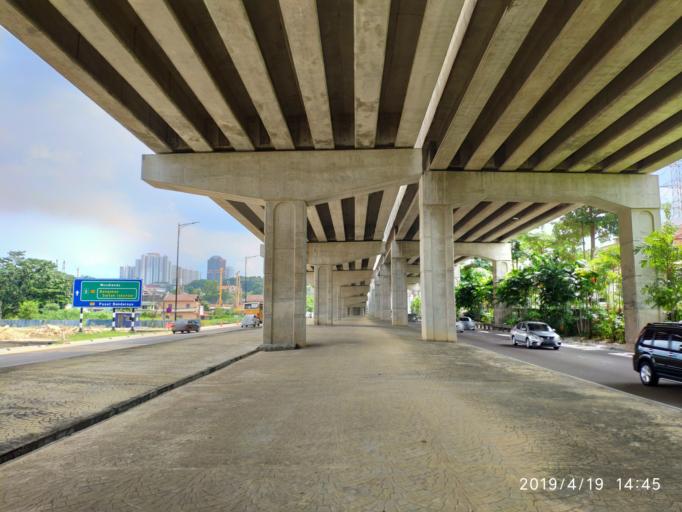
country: MY
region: Johor
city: Johor Bahru
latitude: 1.4723
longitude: 103.7774
